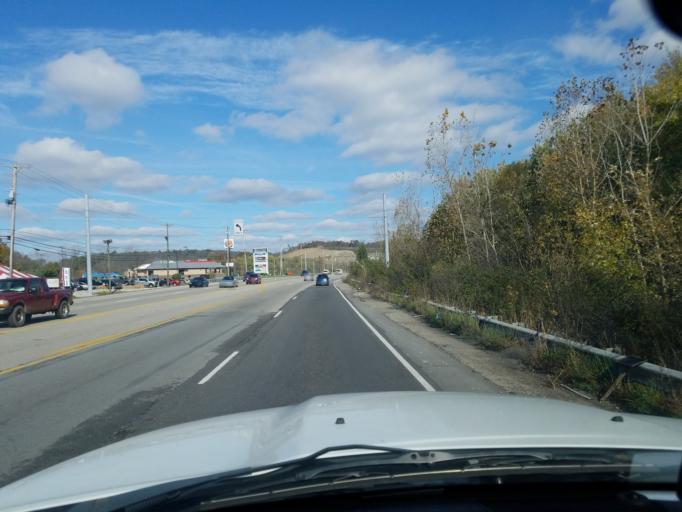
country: US
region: Indiana
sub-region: Dearborn County
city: Aurora
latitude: 39.0733
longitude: -84.8930
